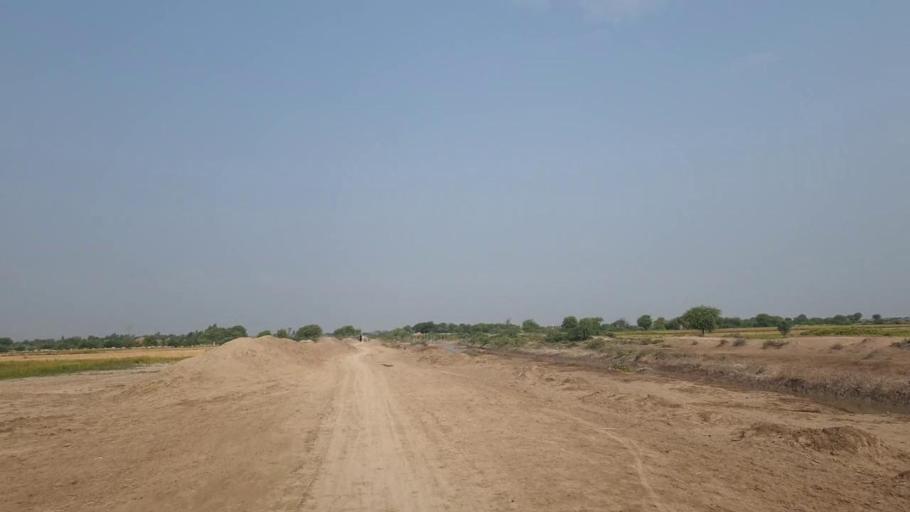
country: PK
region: Sindh
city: Badin
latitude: 24.7309
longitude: 68.7675
